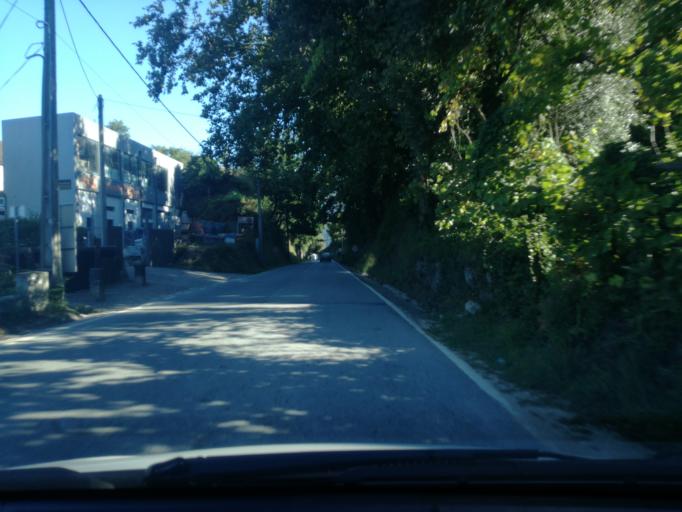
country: PT
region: Braga
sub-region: Vieira do Minho
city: Real
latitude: 41.6721
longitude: -8.1781
